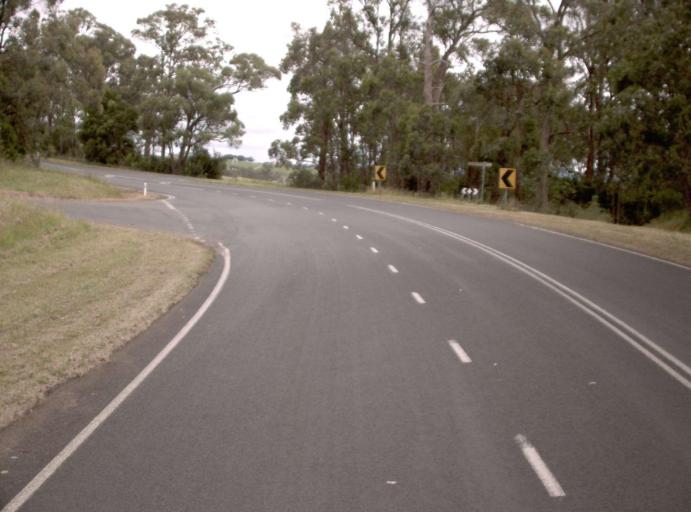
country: AU
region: Victoria
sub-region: Latrobe
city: Moe
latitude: -38.0643
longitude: 146.1738
